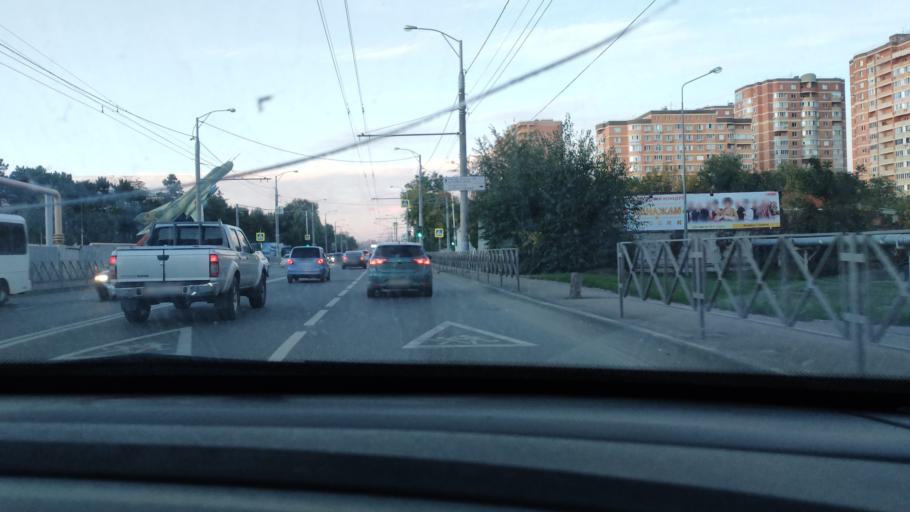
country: RU
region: Krasnodarskiy
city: Krasnodar
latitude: 45.0783
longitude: 38.9745
